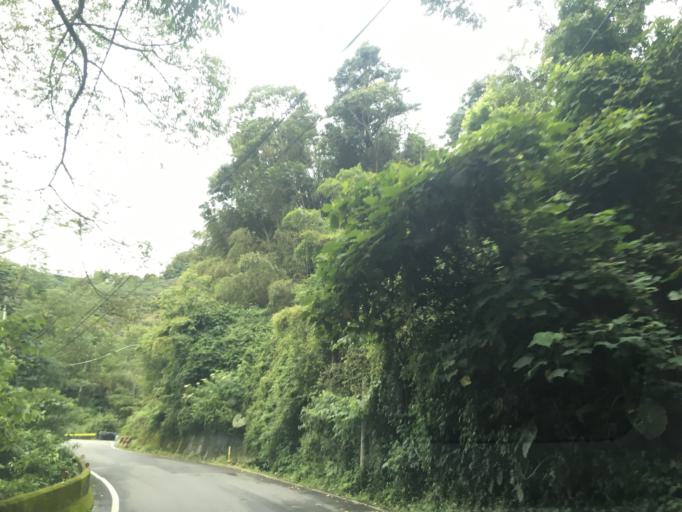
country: TW
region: Taiwan
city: Lugu
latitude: 23.5296
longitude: 120.7060
